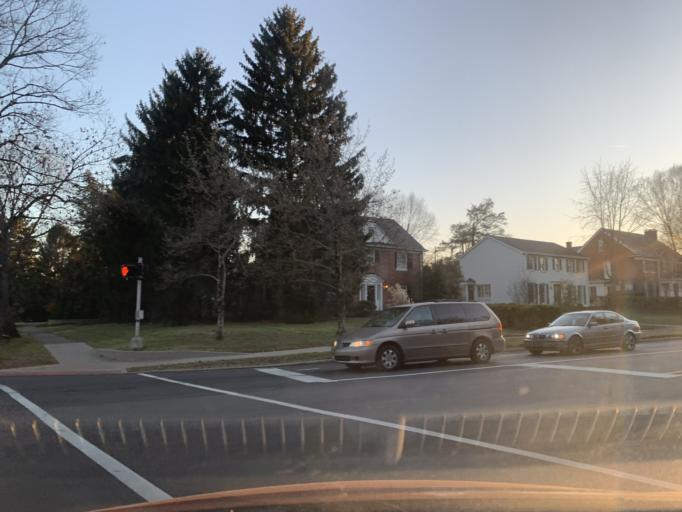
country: US
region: Kentucky
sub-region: Jefferson County
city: Saint Matthews
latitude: 38.2487
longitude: -85.6807
